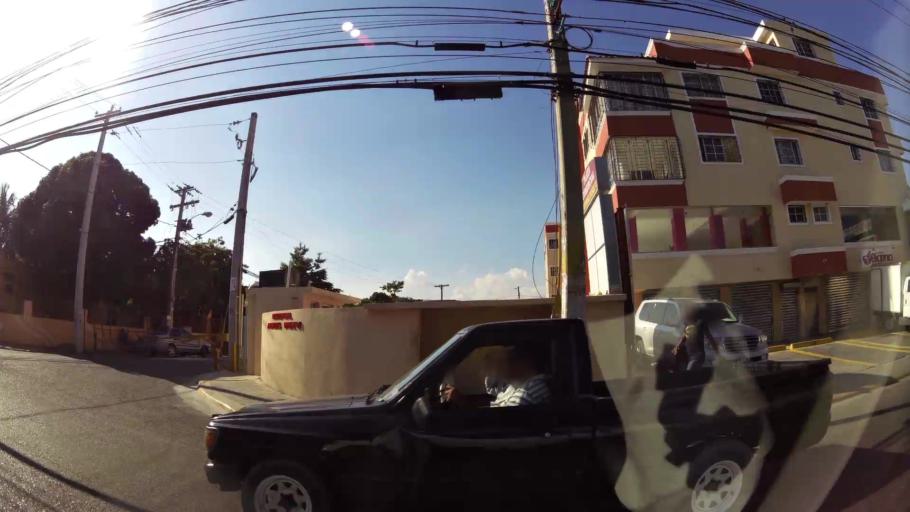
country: DO
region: Nacional
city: Santo Domingo
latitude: 18.4762
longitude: -69.9836
